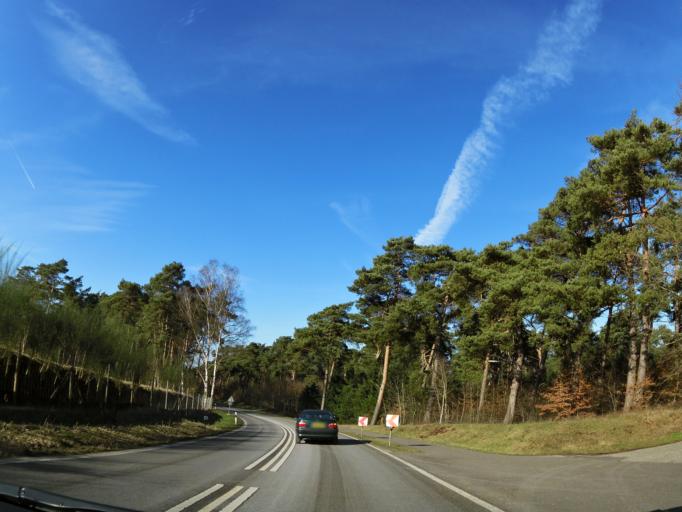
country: DE
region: North Rhine-Westphalia
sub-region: Regierungsbezirk Koln
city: Selfkant
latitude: 51.0068
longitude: 5.9246
